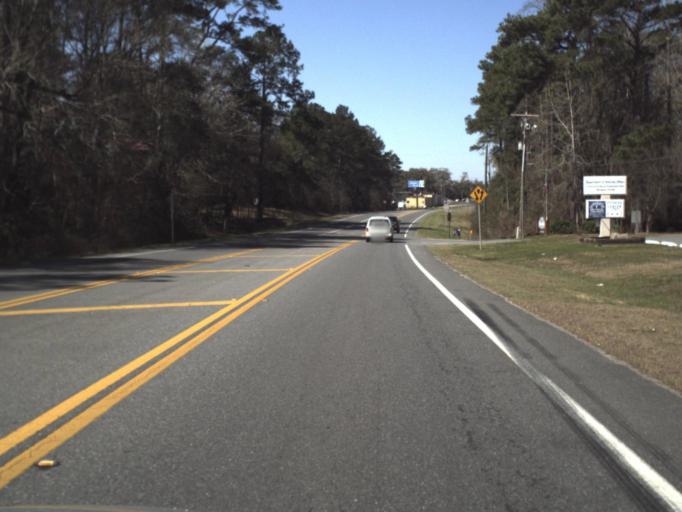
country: US
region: Florida
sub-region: Jackson County
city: Marianna
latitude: 30.7472
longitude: -85.1814
